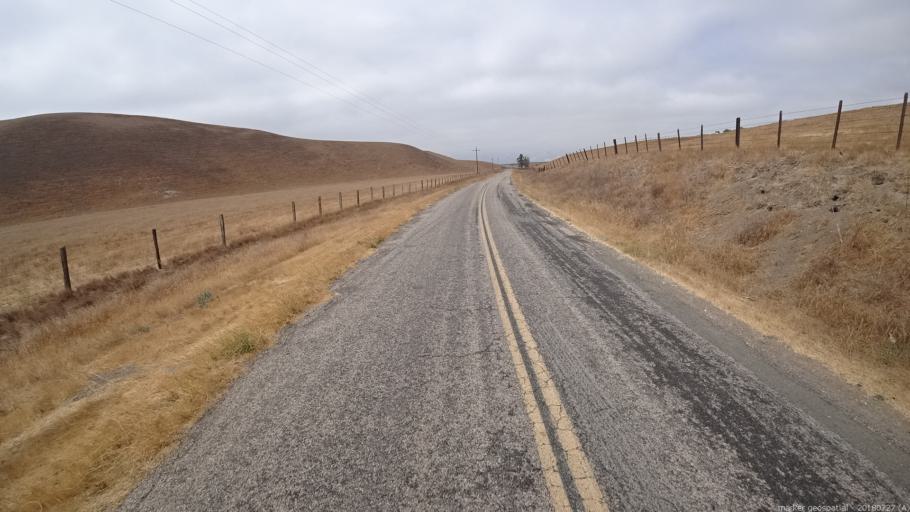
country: US
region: California
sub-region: Monterey County
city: King City
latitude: 36.2233
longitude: -121.0686
